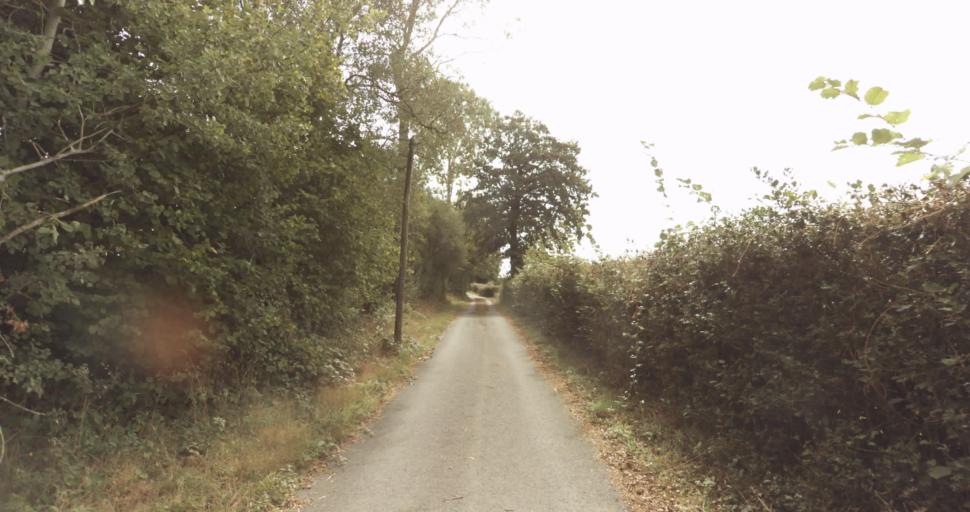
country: FR
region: Lower Normandy
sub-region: Departement du Calvados
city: Orbec
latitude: 48.9456
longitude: 0.3947
